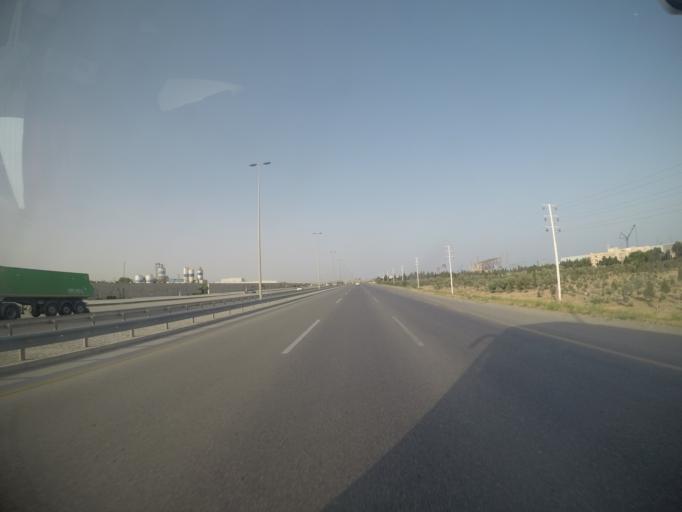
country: AZ
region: Baki
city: Puta
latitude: 40.2615
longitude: 49.6477
